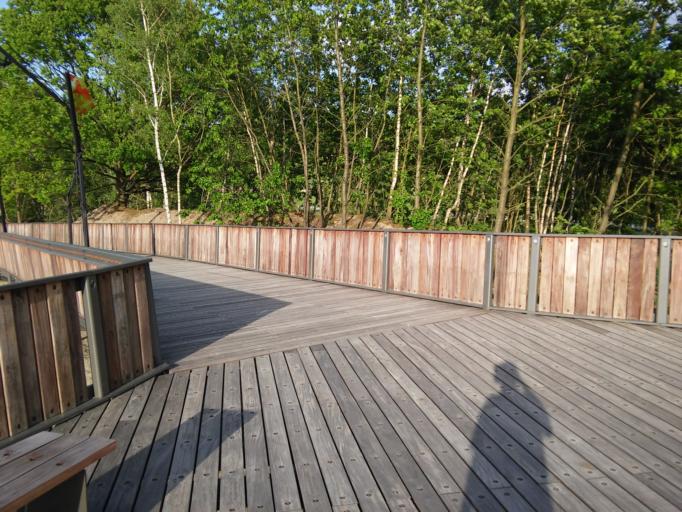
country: BE
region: Flanders
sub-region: Provincie Antwerpen
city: Boom
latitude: 51.0907
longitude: 4.3829
